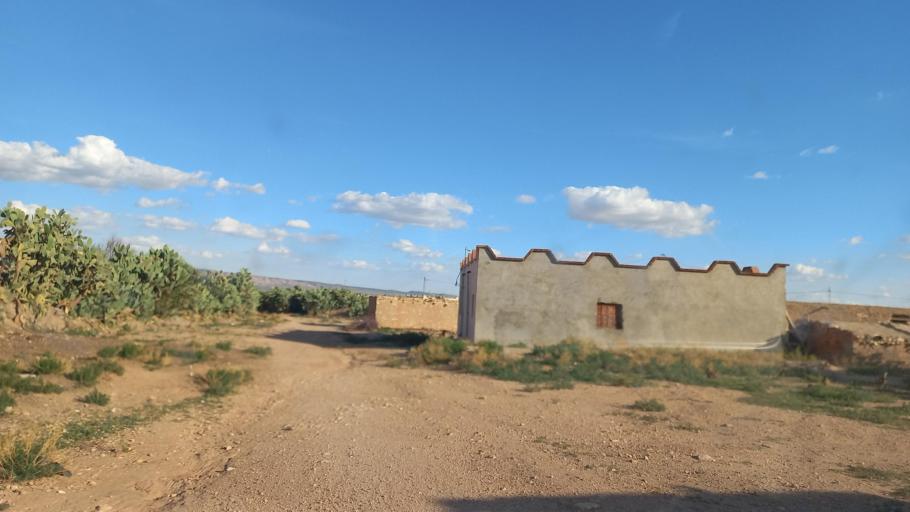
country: TN
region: Al Qasrayn
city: Sbiba
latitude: 35.3809
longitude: 9.0216
